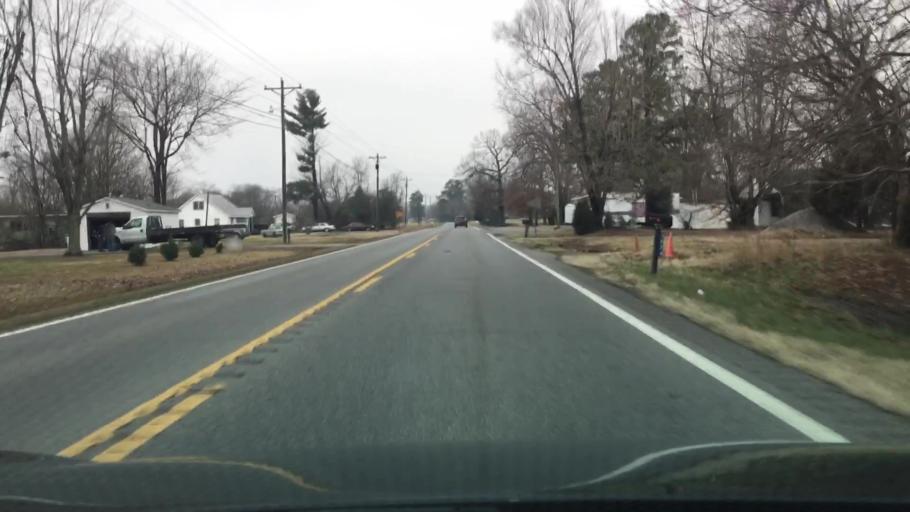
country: US
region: Kentucky
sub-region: Marshall County
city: Calvert City
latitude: 36.9697
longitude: -88.3885
